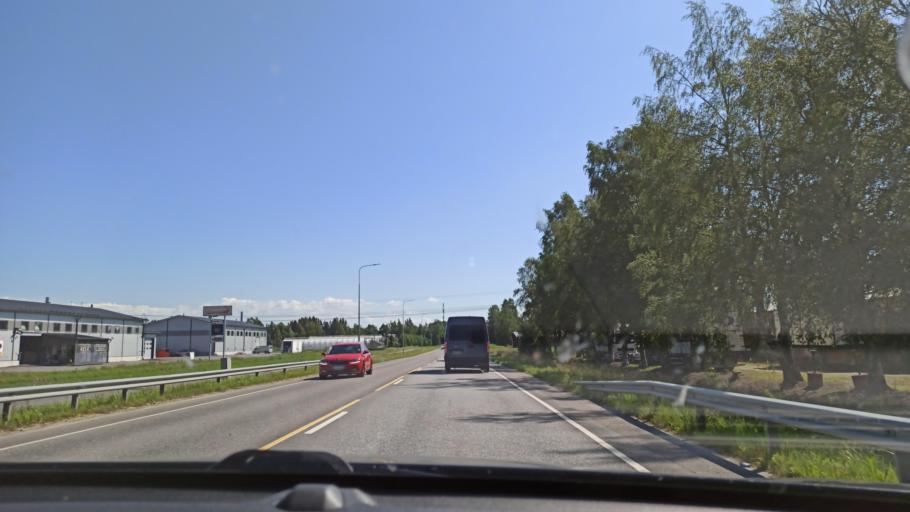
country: FI
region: Satakunta
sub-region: Pori
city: Pori
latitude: 61.5102
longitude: 21.8033
